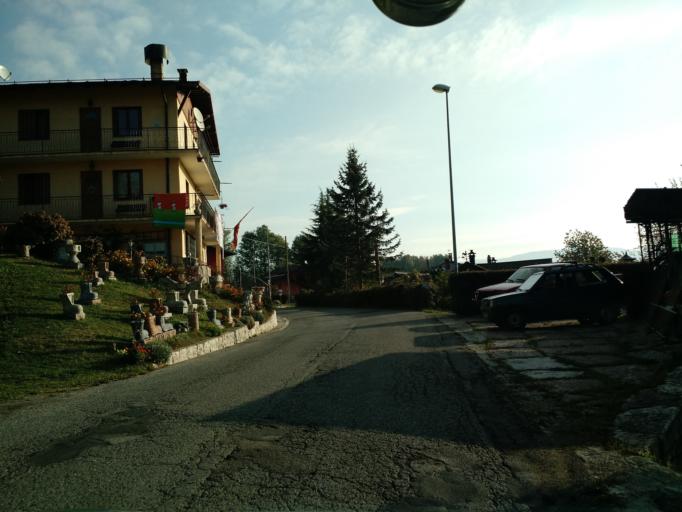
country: IT
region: Veneto
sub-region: Provincia di Vicenza
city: Foza
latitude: 45.8651
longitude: 11.6168
